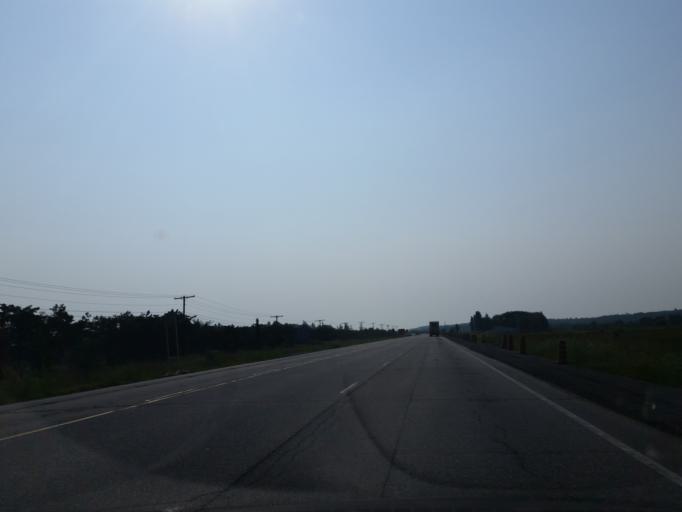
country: CA
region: Ontario
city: Greater Sudbury
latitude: 46.4323
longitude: -80.2573
